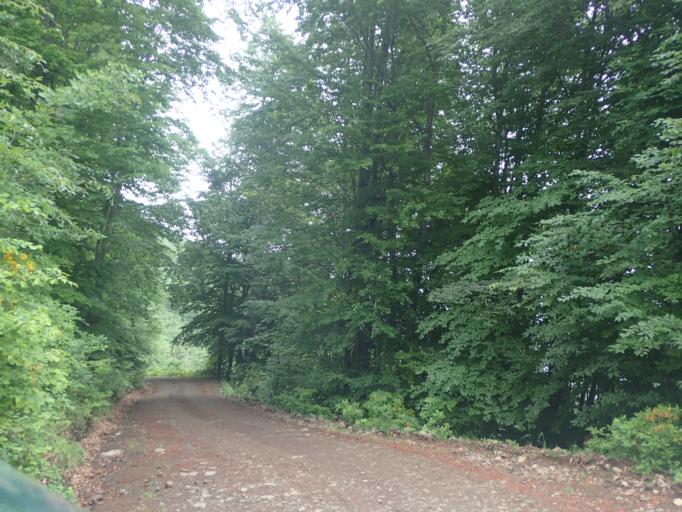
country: TR
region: Samsun
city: Salipazari
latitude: 40.9299
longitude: 36.8877
